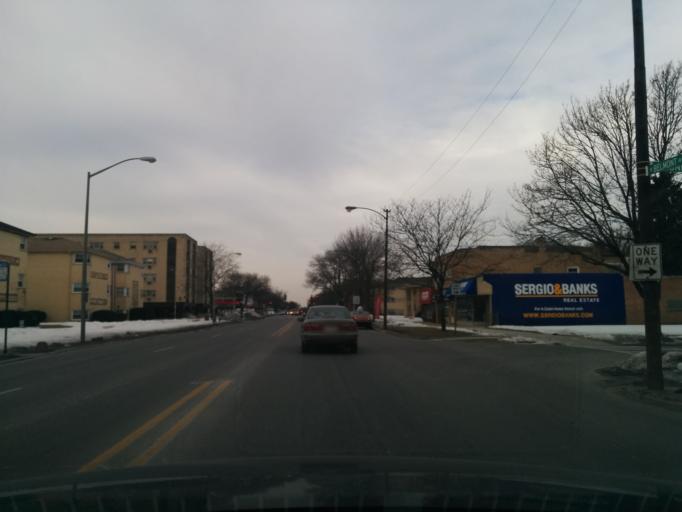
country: US
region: Illinois
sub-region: Cook County
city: River Grove
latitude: 41.9377
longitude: -87.8309
